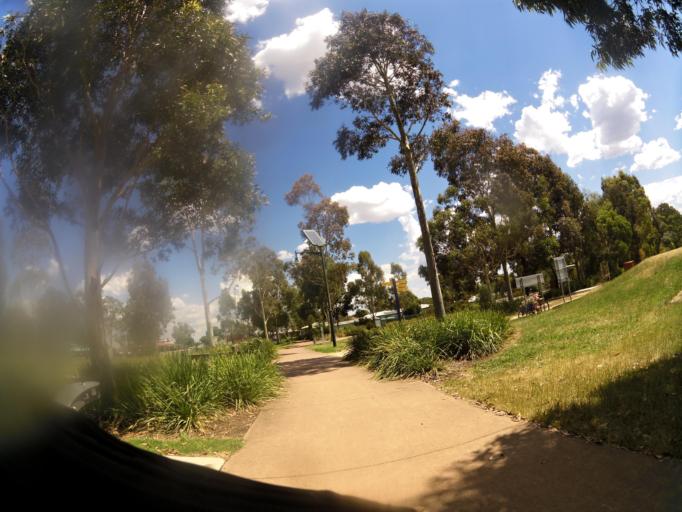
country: AU
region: Victoria
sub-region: Wellington
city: Heyfield
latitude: -37.9794
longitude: 146.7870
